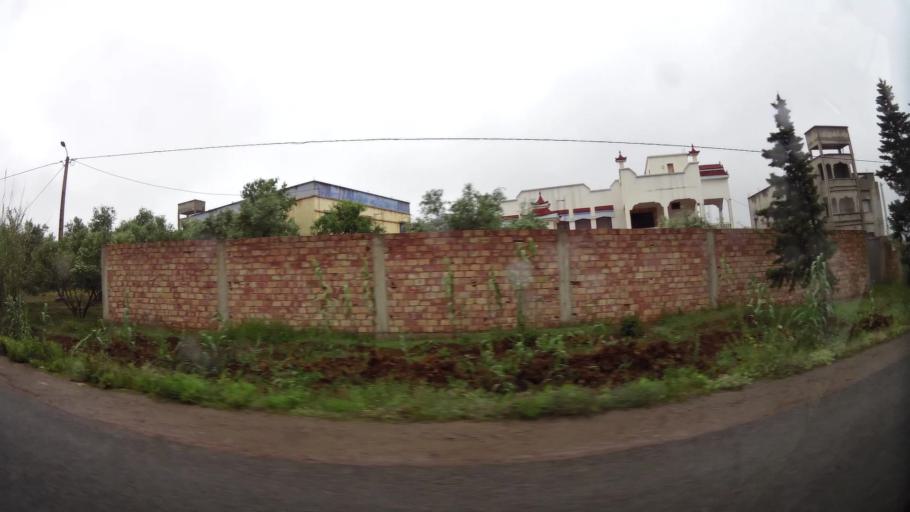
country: MA
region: Oriental
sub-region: Nador
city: Boudinar
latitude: 35.1149
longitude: -3.5761
